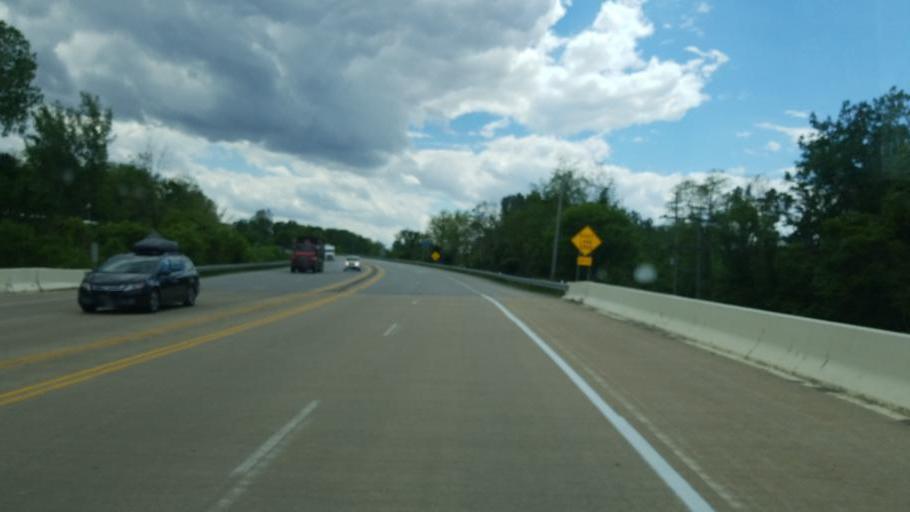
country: US
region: Ohio
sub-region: Erie County
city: Milan
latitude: 41.3011
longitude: -82.6097
